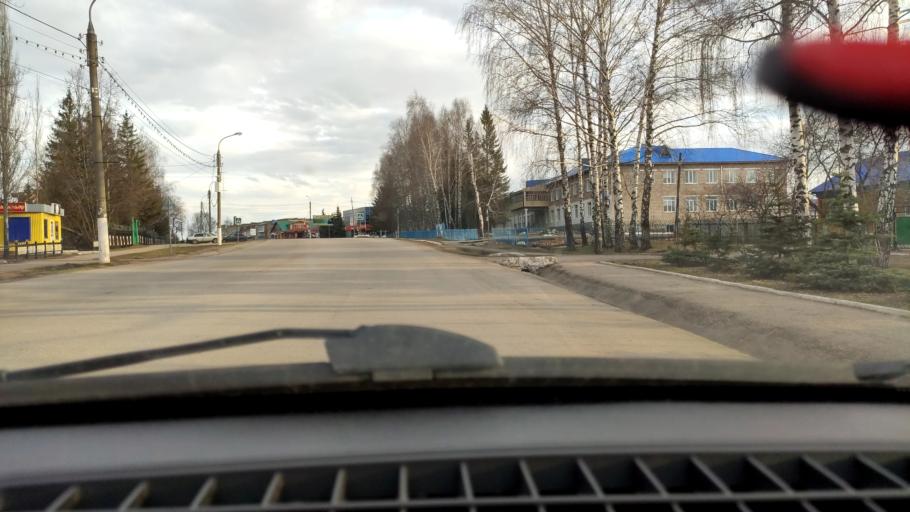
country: RU
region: Bashkortostan
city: Tolbazy
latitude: 54.0125
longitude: 55.8863
